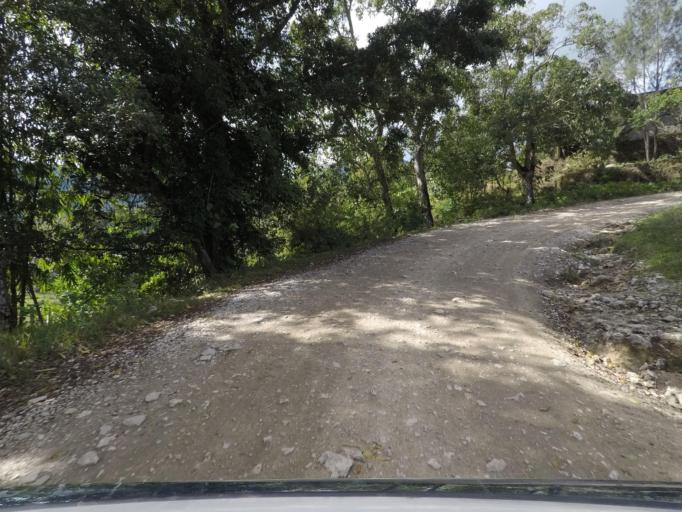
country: TL
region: Baucau
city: Venilale
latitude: -8.6849
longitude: 126.3733
